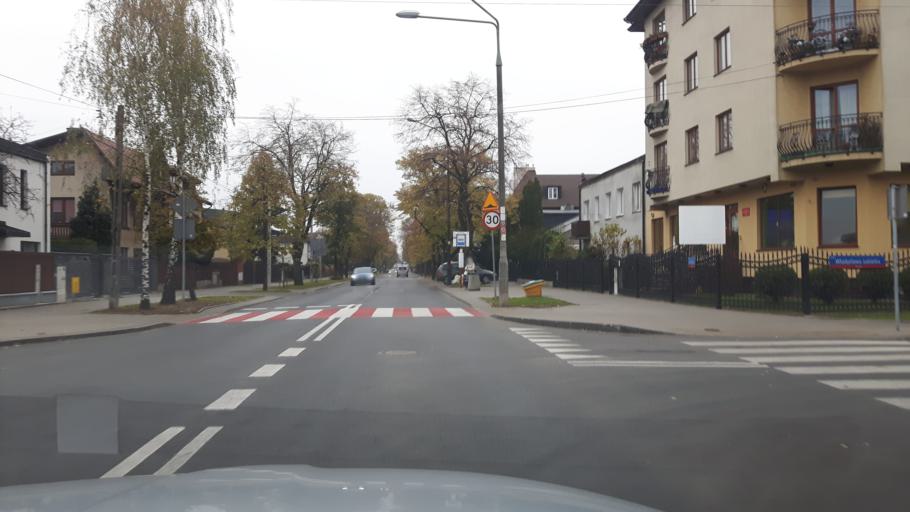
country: PL
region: Masovian Voivodeship
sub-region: Warszawa
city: Targowek
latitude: 52.2789
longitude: 21.0607
